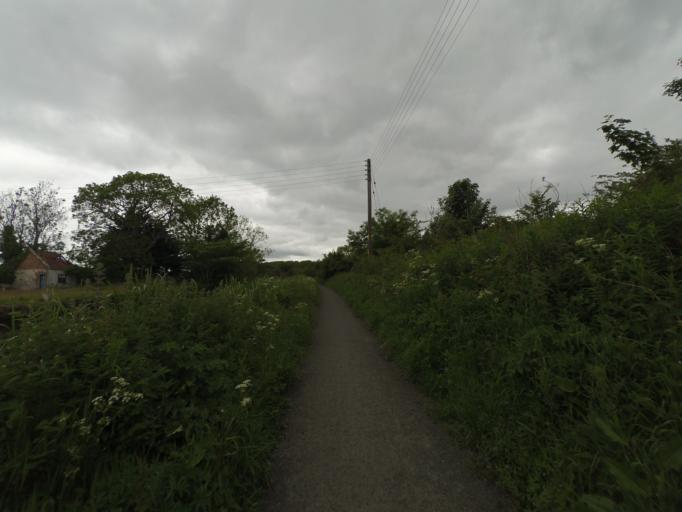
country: GB
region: Scotland
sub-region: West Lothian
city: Broxburn
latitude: 55.9624
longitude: -3.4640
